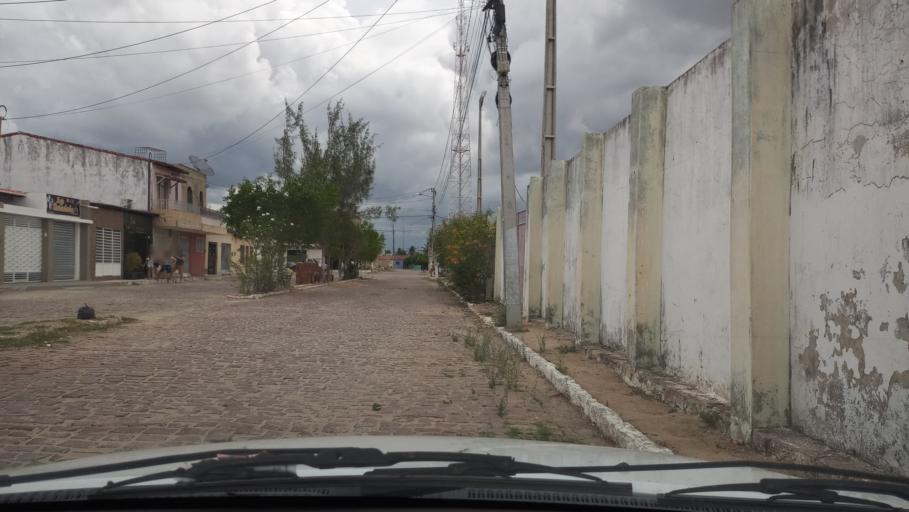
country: BR
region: Rio Grande do Norte
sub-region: Tangara
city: Tangara
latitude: -6.1972
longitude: -35.7999
